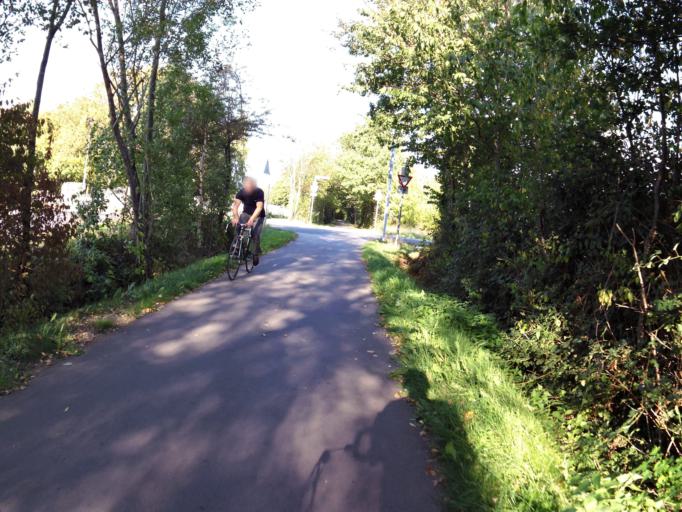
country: DE
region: North Rhine-Westphalia
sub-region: Regierungsbezirk Koln
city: Wurselen
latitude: 50.7600
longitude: 6.1618
